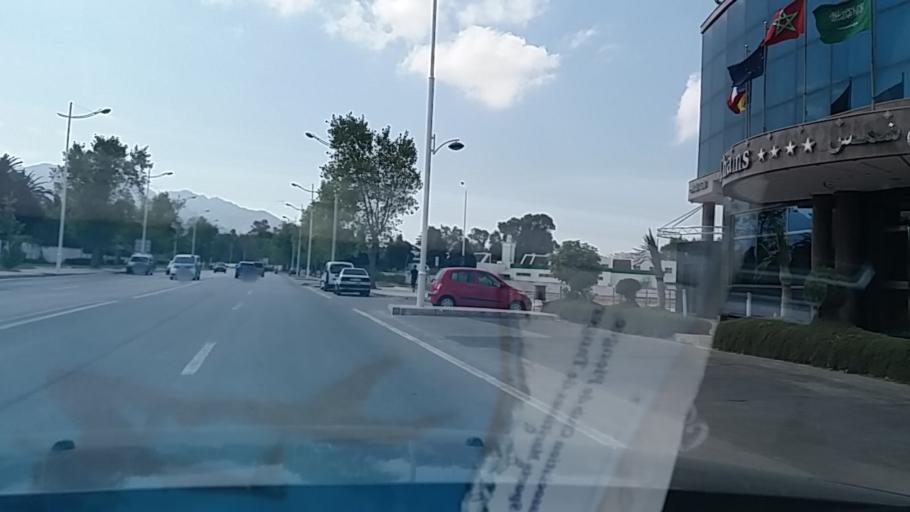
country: MA
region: Tanger-Tetouan
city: Tetouan
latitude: 35.5810
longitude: -5.3361
